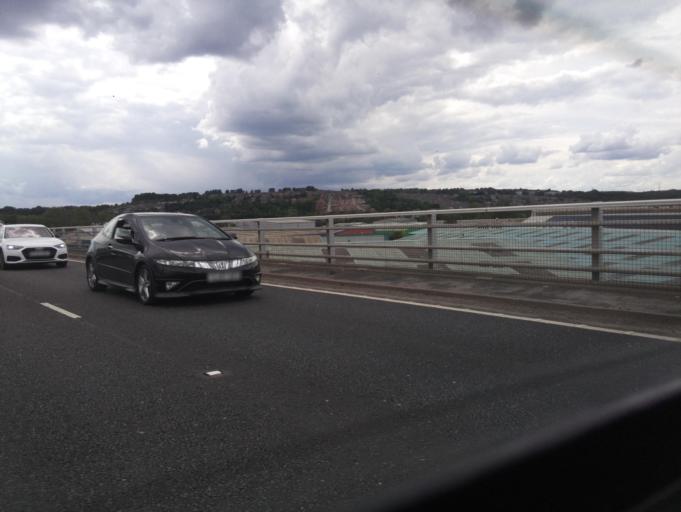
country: GB
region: England
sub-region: Gateshead
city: Blaydon-on-Tyne
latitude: 54.9685
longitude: -1.6961
